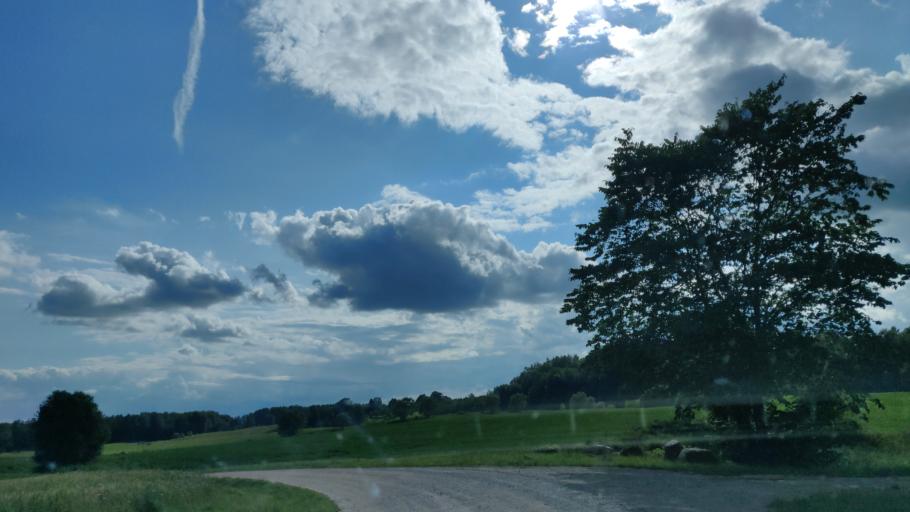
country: LT
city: Varniai
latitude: 55.6075
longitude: 22.3236
